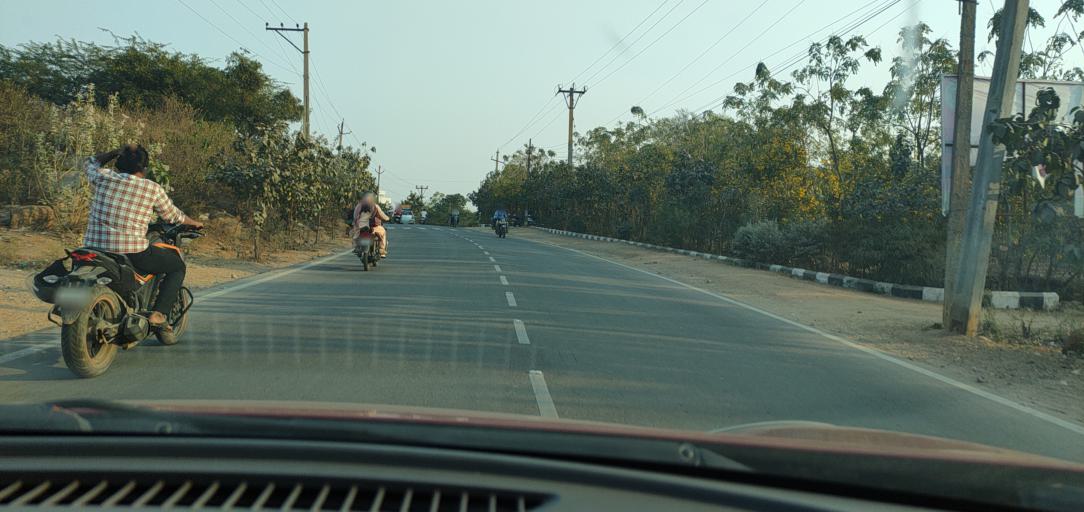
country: IN
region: Telangana
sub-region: Rangareddi
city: Uppal Kalan
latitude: 17.4316
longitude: 78.5786
